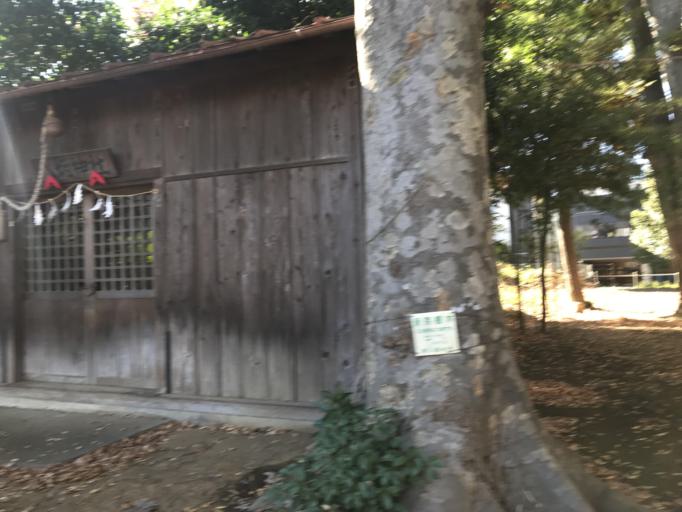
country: JP
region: Tokyo
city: Tanashicho
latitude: 35.7527
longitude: 139.5121
